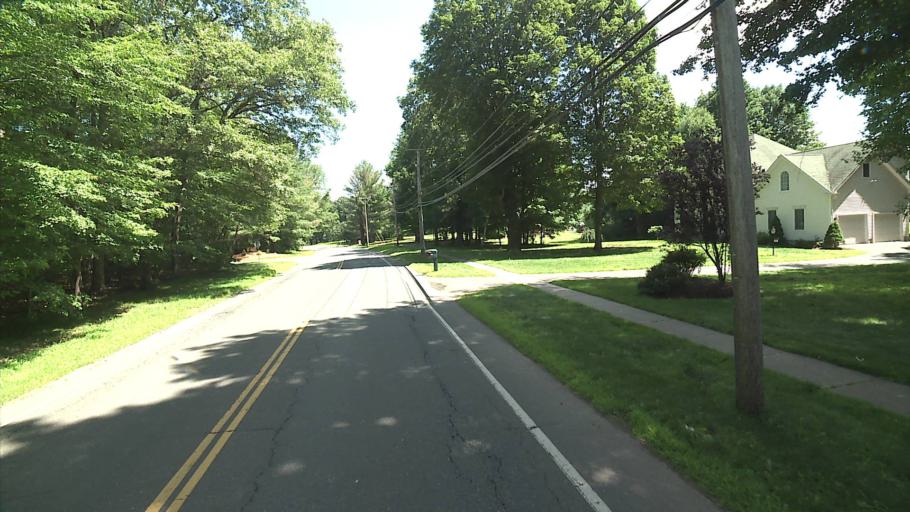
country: US
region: Connecticut
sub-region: Hartford County
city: Suffield Depot
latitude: 41.9842
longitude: -72.6832
